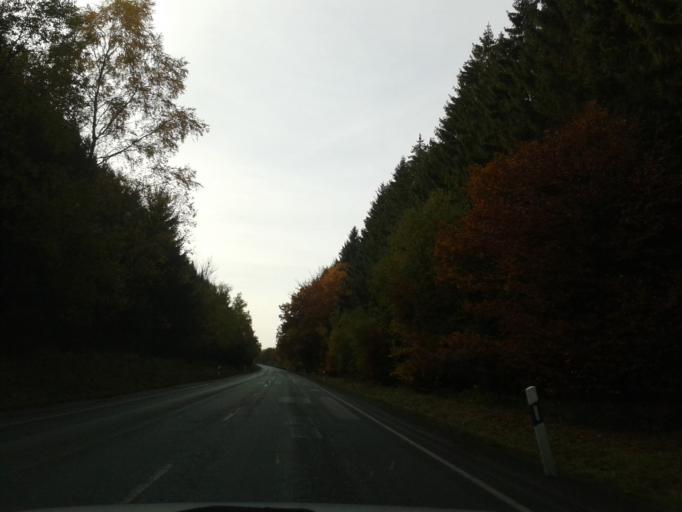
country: DE
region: North Rhine-Westphalia
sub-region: Regierungsbezirk Arnsberg
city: Ruthen
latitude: 51.4259
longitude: 8.4357
